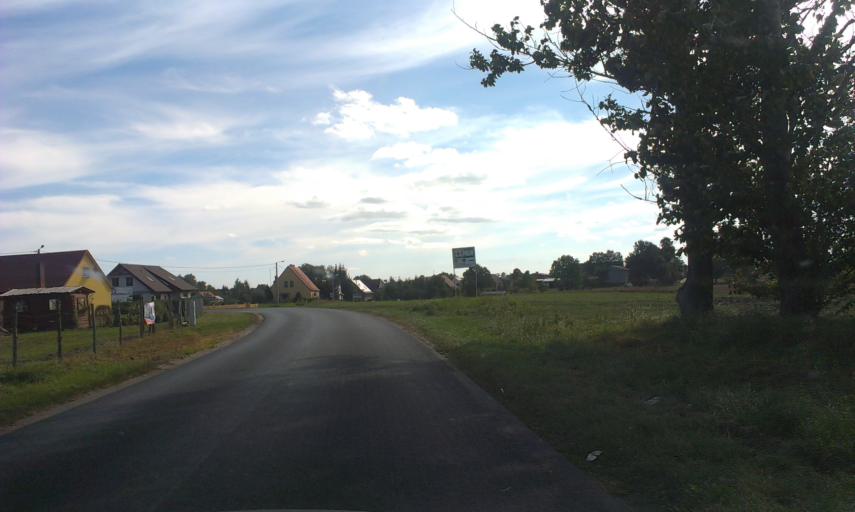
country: PL
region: Greater Poland Voivodeship
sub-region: Powiat zlotowski
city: Zlotow
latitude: 53.3099
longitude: 17.1249
